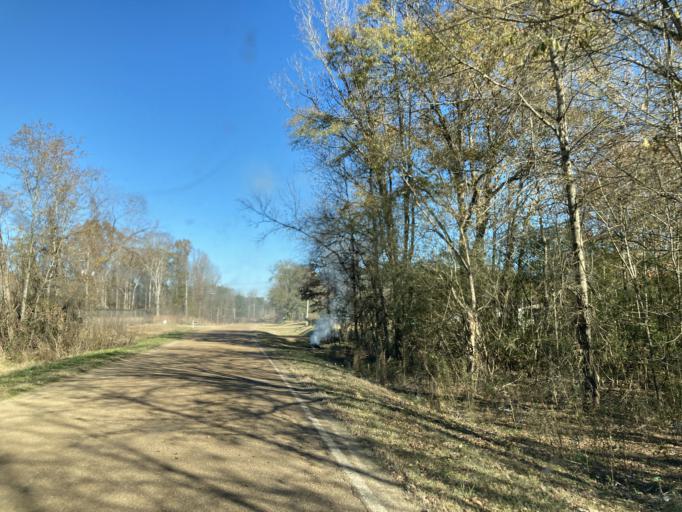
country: US
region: Mississippi
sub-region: Holmes County
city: Pickens
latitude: 32.8549
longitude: -90.0150
